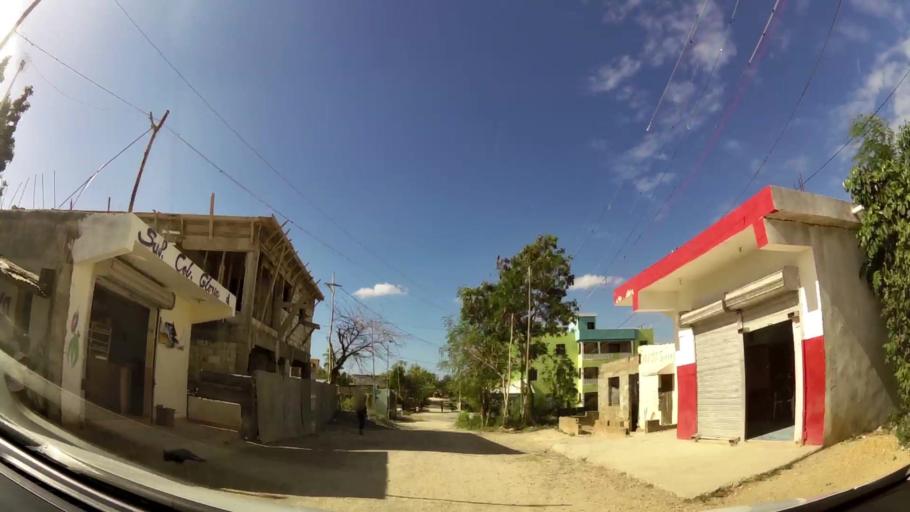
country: DO
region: Santo Domingo
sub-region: Santo Domingo
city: Boca Chica
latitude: 18.4621
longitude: -69.6021
